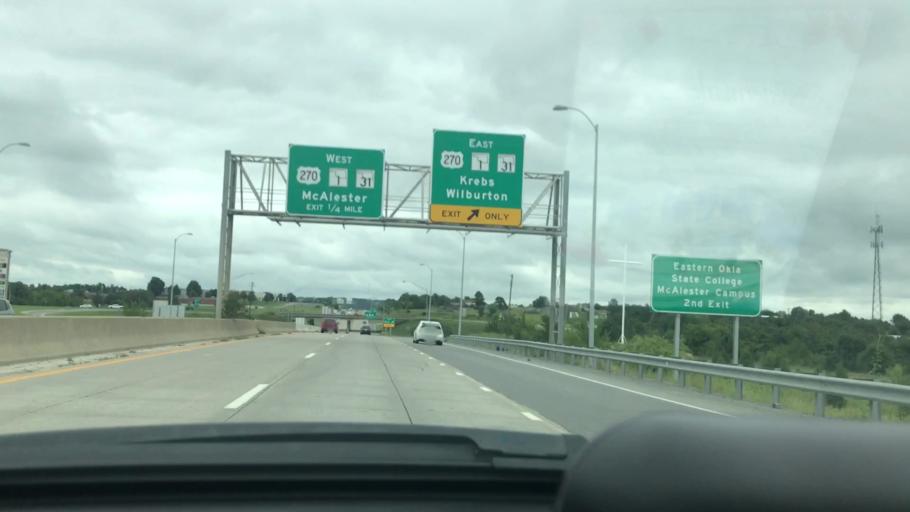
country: US
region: Oklahoma
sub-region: Pittsburg County
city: Krebs
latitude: 34.9243
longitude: -95.7423
